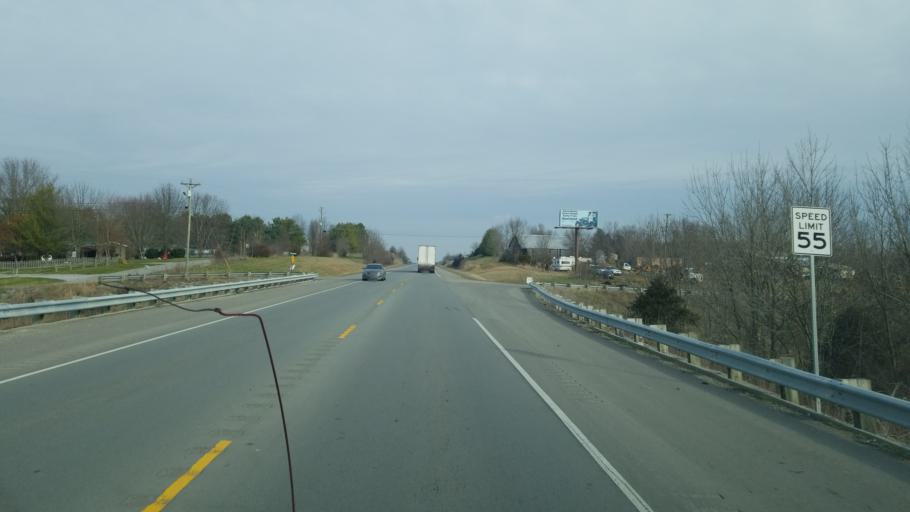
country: US
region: Kentucky
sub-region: Boyle County
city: Junction City
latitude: 37.5413
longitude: -84.8030
